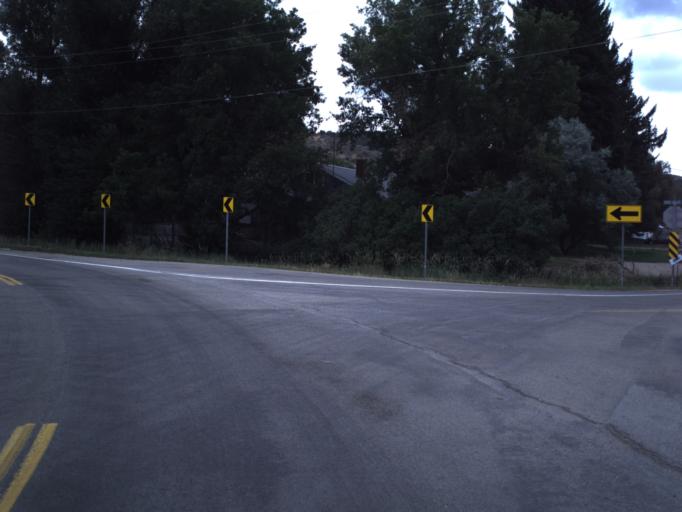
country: US
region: Utah
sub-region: Summit County
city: Oakley
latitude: 40.7250
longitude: -111.3418
